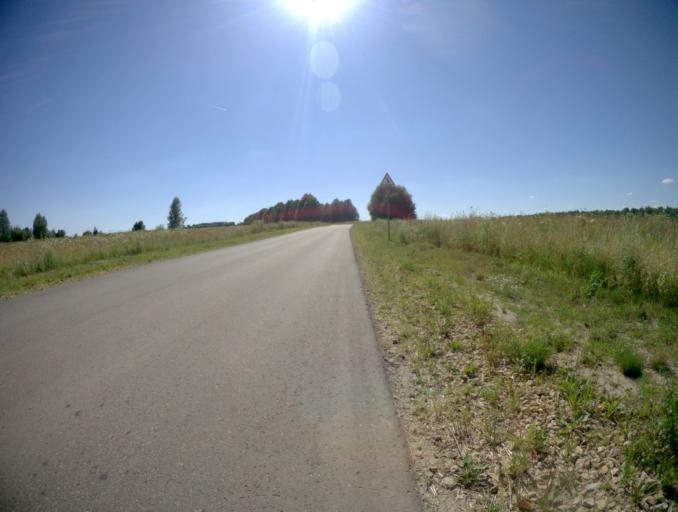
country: RU
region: Nizjnij Novgorod
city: Vorsma
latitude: 56.0346
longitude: 43.1815
